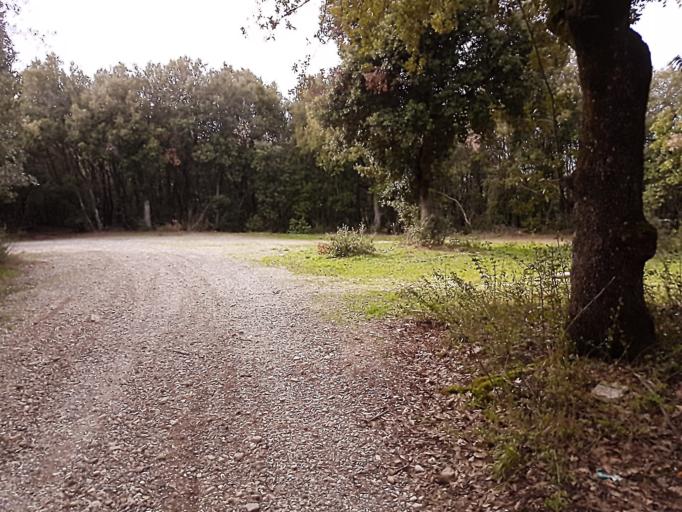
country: IT
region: Umbria
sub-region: Provincia di Perugia
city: Corciano
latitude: 43.1347
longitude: 12.3001
